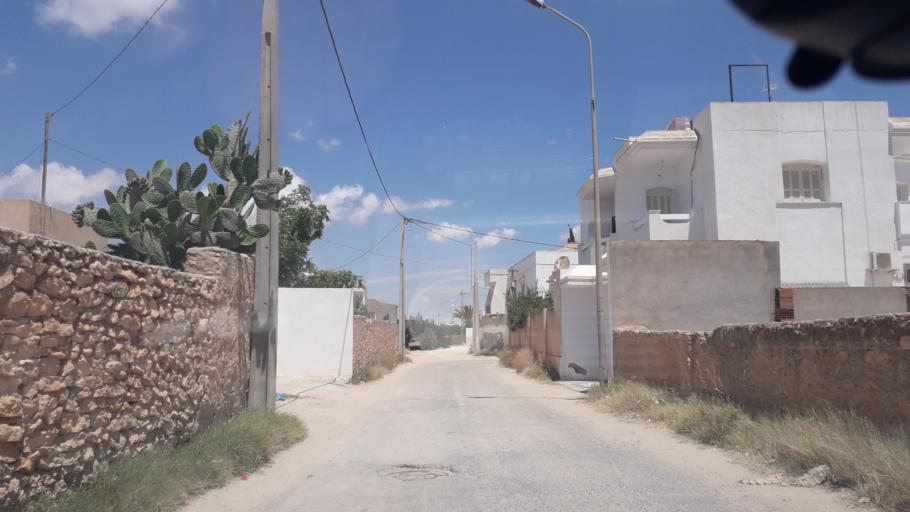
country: TN
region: Safaqis
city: Al Qarmadah
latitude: 34.8162
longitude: 10.7652
